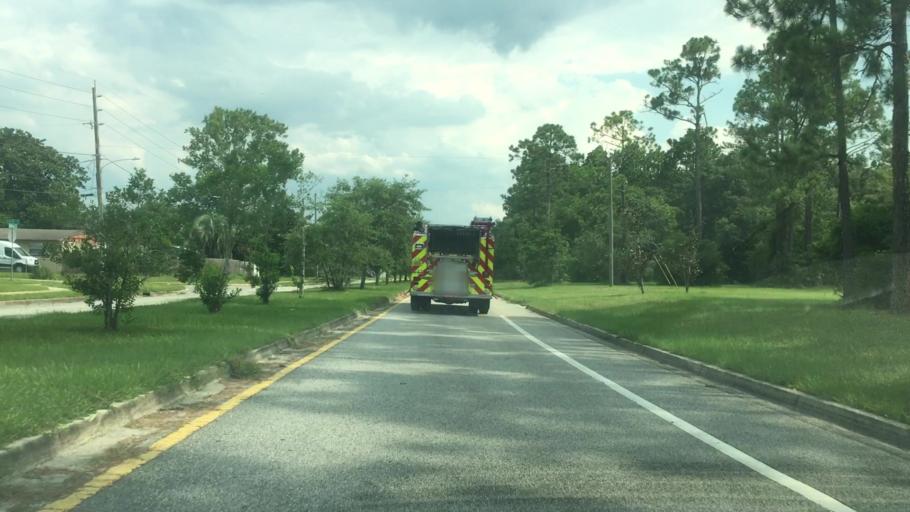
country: US
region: Florida
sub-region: Duval County
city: Neptune Beach
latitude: 30.2905
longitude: -81.5051
